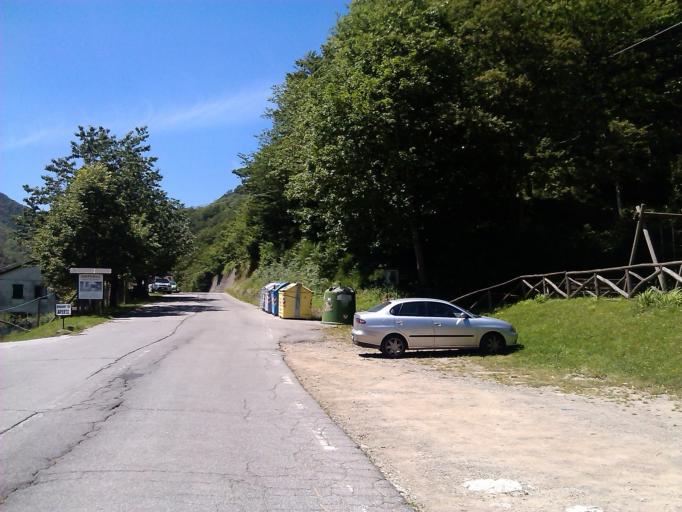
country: IT
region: Tuscany
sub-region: Provincia di Prato
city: Cantagallo
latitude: 44.0264
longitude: 11.0355
